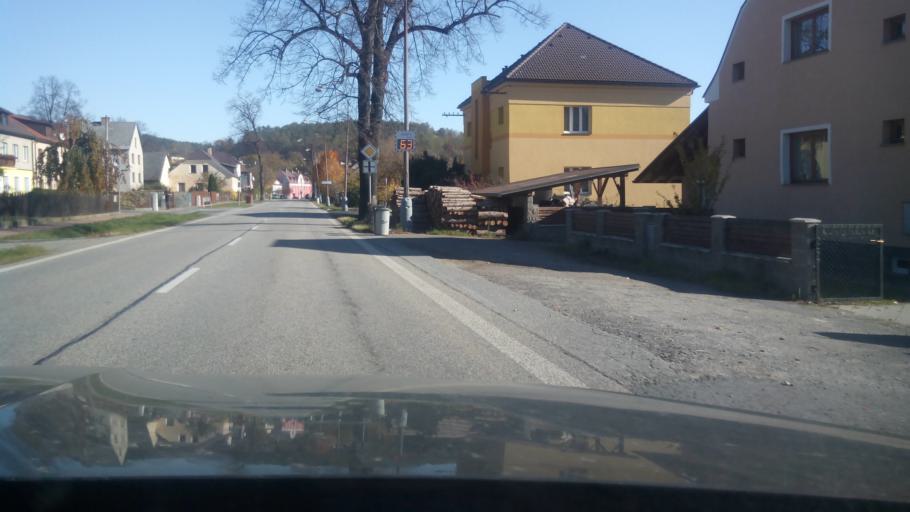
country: CZ
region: Jihocesky
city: Ckyne
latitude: 49.1135
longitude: 13.8239
